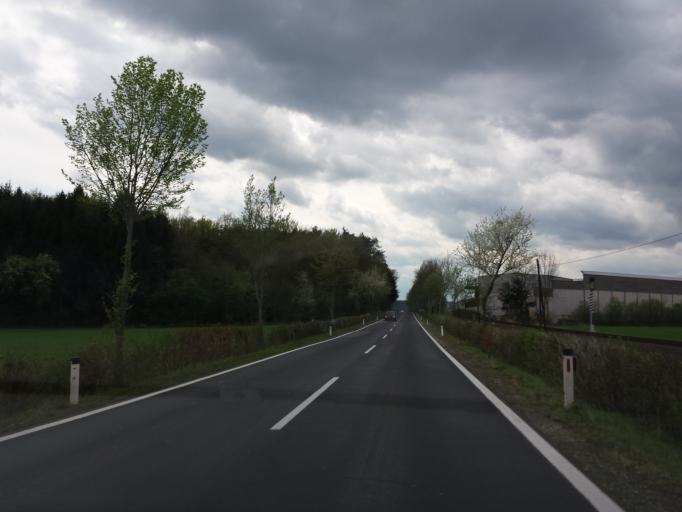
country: AT
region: Styria
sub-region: Politischer Bezirk Hartberg-Fuerstenfeld
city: Fuerstenfeld
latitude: 47.0270
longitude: 16.0750
